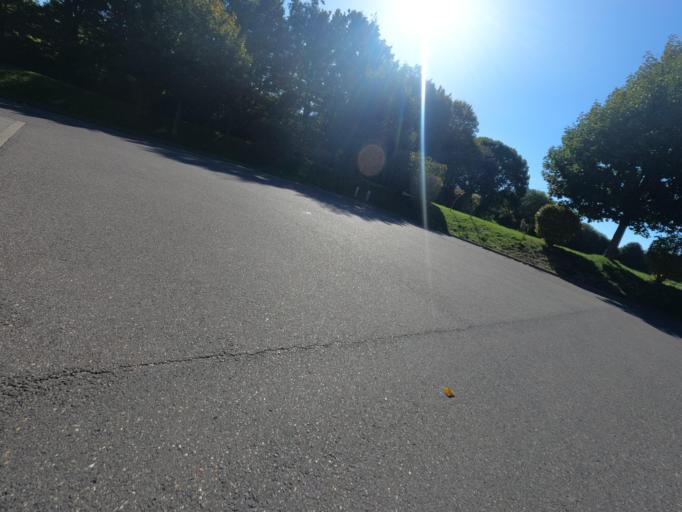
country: DE
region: North Rhine-Westphalia
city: Erkelenz
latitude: 51.0641
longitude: 6.3382
